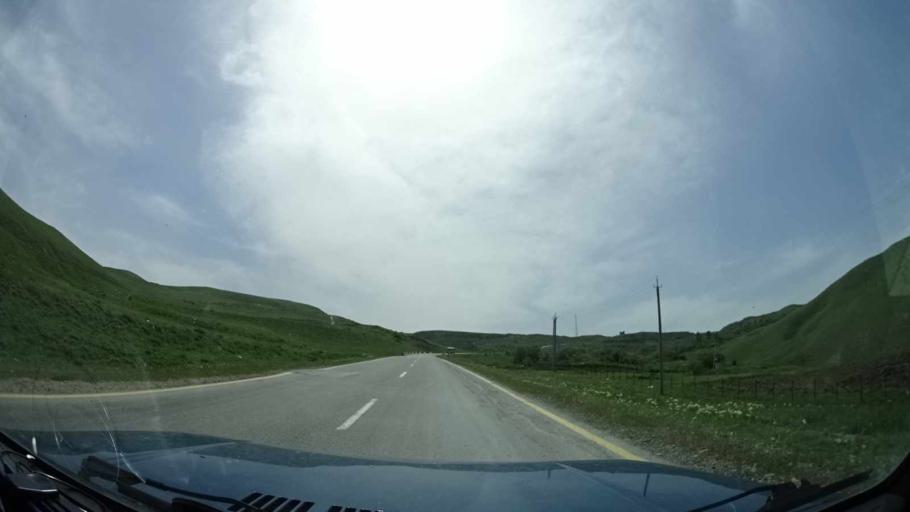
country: AZ
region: Xizi
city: Khyzy
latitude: 40.9060
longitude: 49.1223
